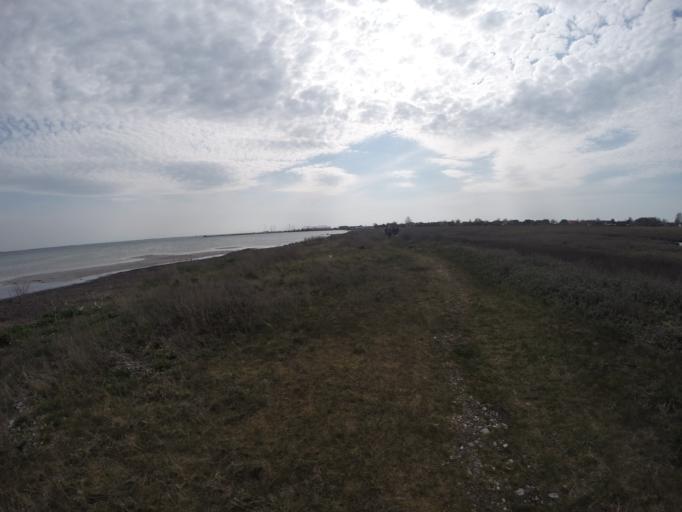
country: DK
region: Zealand
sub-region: Kalundborg Kommune
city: Gorlev
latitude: 55.5220
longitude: 11.1220
